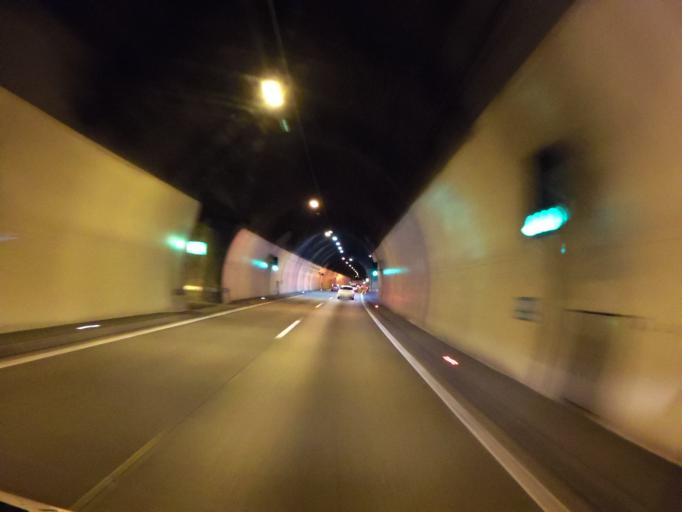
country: AT
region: Styria
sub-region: Politischer Bezirk Graz-Umgebung
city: Deutschfeistritz
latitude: 47.1945
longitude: 15.3254
